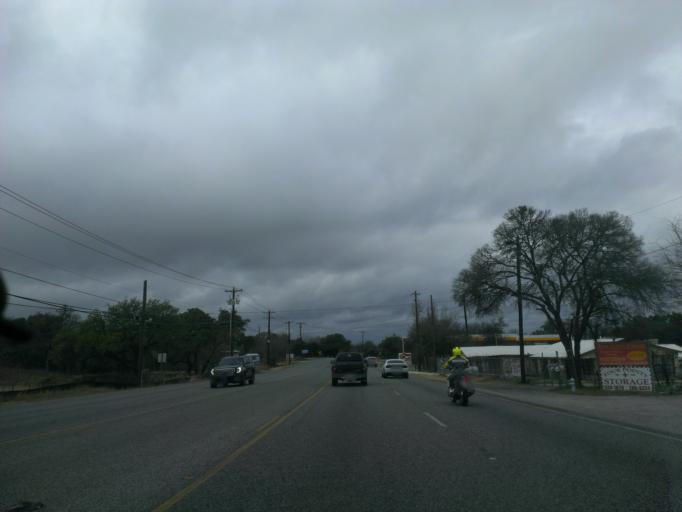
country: US
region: Texas
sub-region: Williamson County
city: Anderson Mill
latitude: 30.3959
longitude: -97.8474
